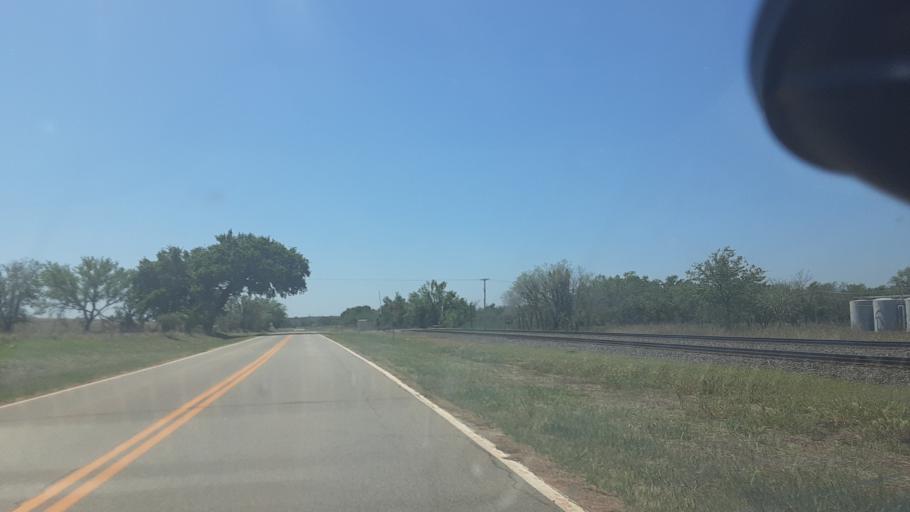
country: US
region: Oklahoma
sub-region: Logan County
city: Guthrie
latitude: 36.0735
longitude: -97.4049
